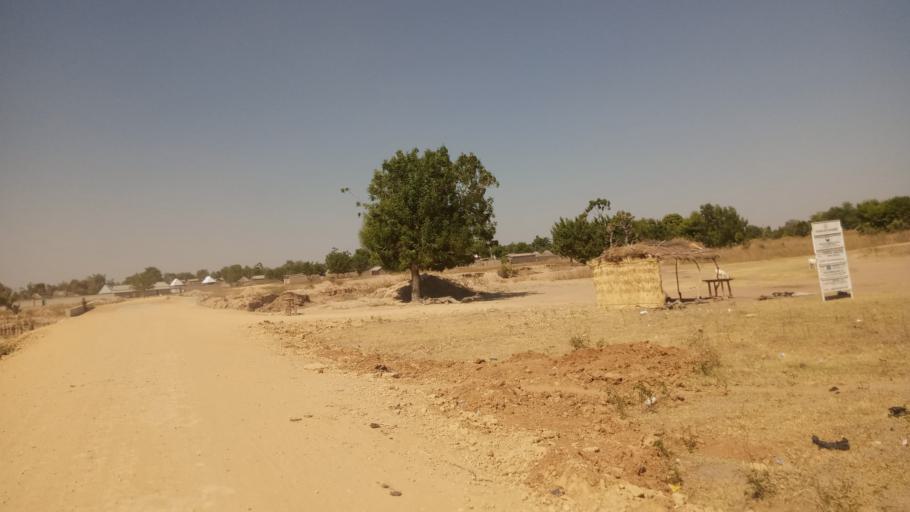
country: NG
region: Adamawa
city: Ngurore
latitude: 9.2977
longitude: 12.1391
